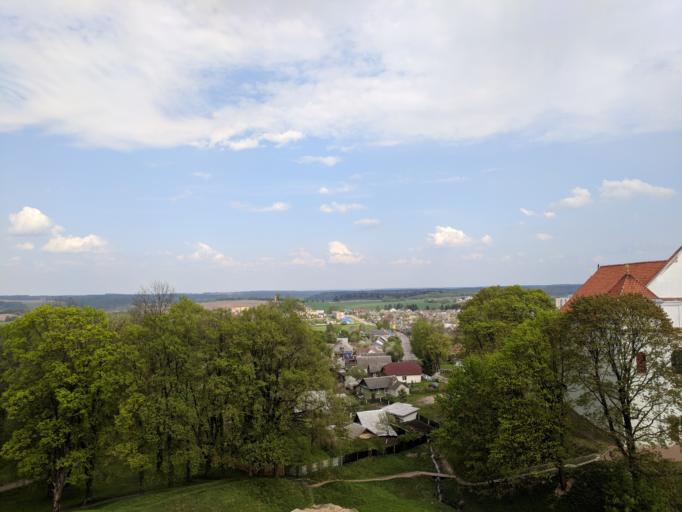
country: BY
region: Grodnenskaya
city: Navahrudak
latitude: 53.6015
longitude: 25.8278
